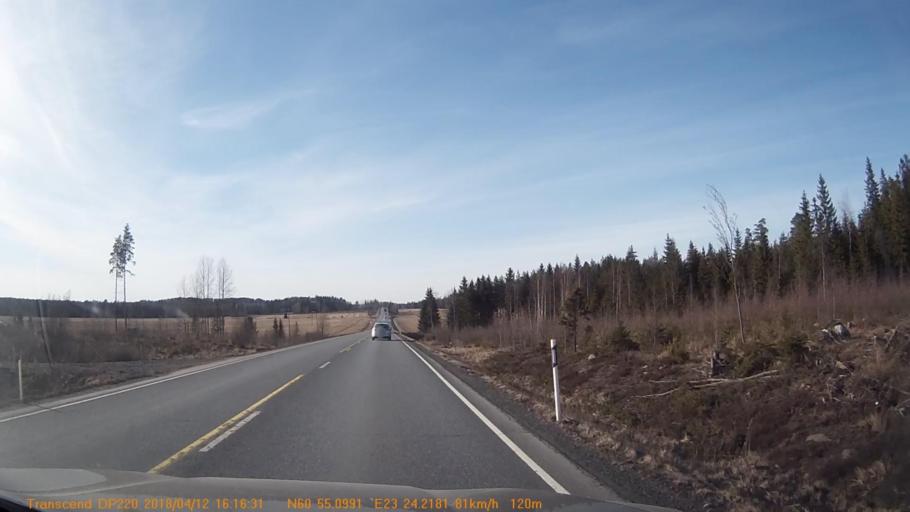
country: FI
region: Haeme
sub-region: Forssa
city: Humppila
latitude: 60.9184
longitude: 23.4035
